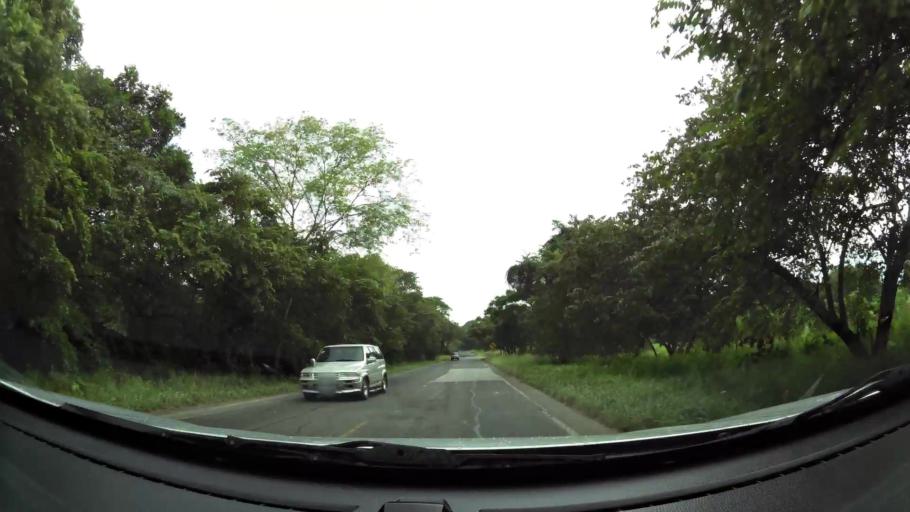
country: CR
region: Guanacaste
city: Juntas
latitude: 10.2030
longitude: -84.9589
